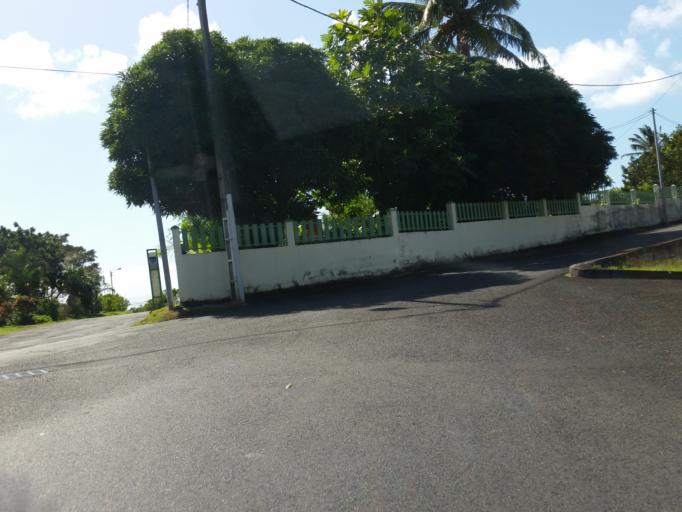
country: RE
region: Reunion
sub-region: Reunion
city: Sainte-Marie
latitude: -20.8985
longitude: 55.5288
